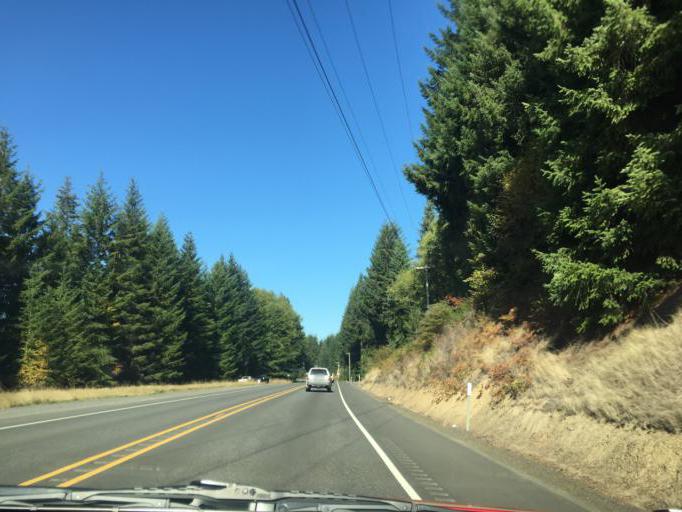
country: US
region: Oregon
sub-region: Columbia County
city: Vernonia
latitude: 45.7331
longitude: -123.2557
